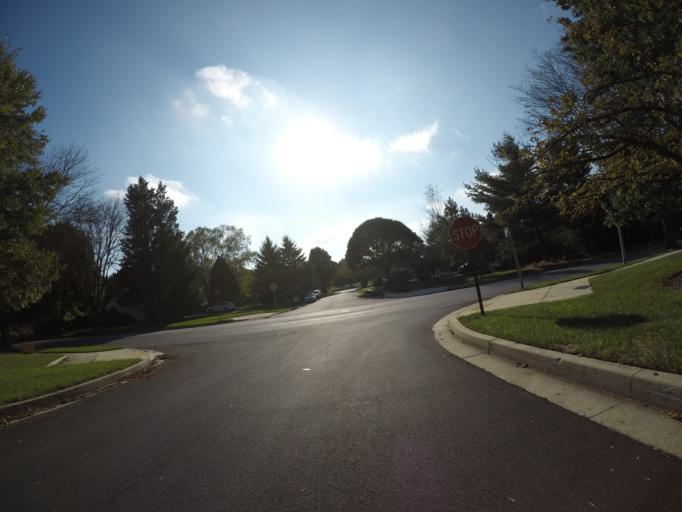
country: US
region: Maryland
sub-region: Howard County
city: Columbia
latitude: 39.2690
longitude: -76.8447
